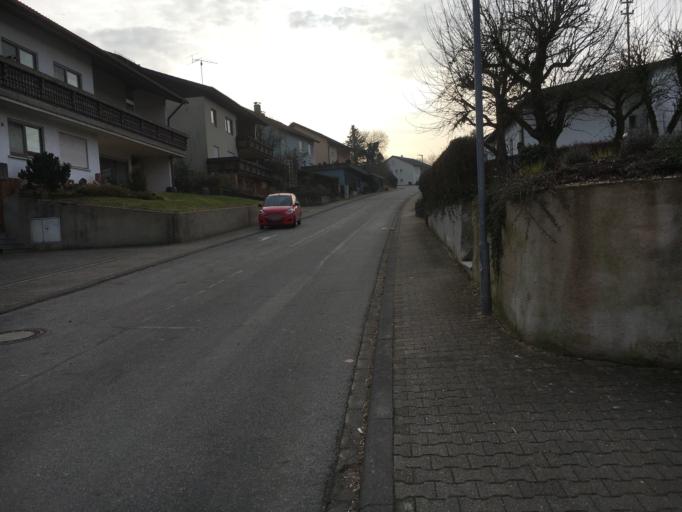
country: DE
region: Baden-Wuerttemberg
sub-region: Karlsruhe Region
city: Limbach
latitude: 49.4232
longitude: 9.2377
